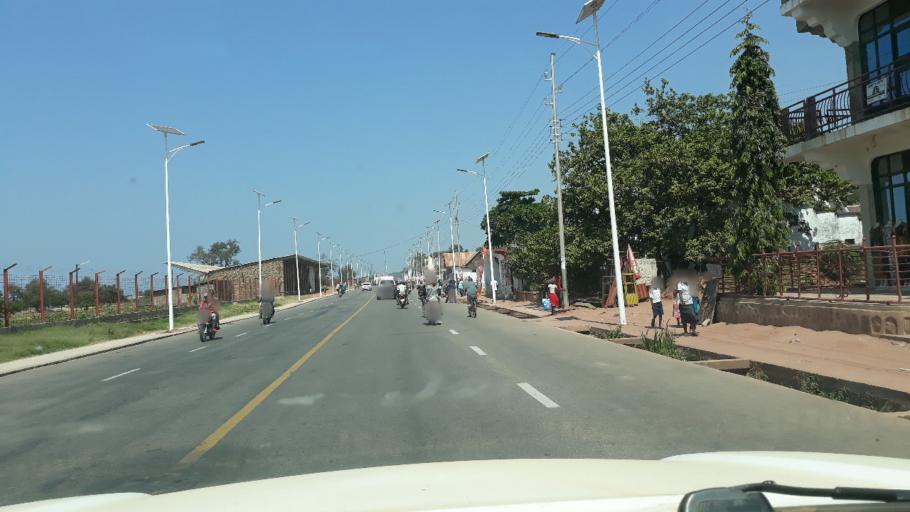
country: CD
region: Katanga
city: Kalemie
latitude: -5.9242
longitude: 29.1918
